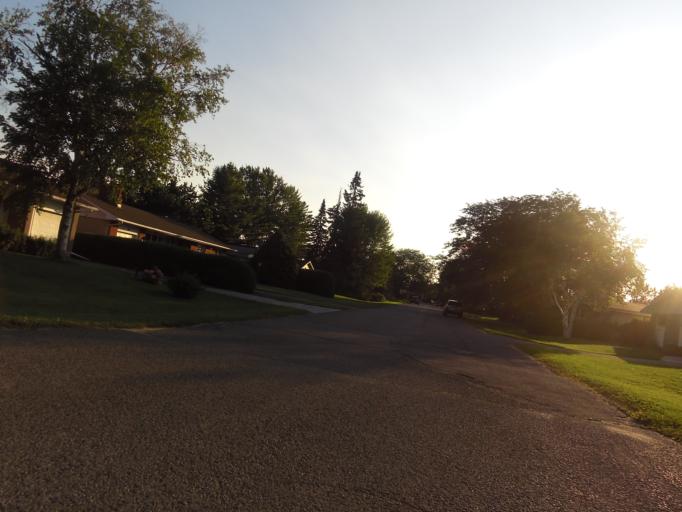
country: CA
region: Ontario
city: Bells Corners
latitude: 45.3182
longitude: -75.8231
